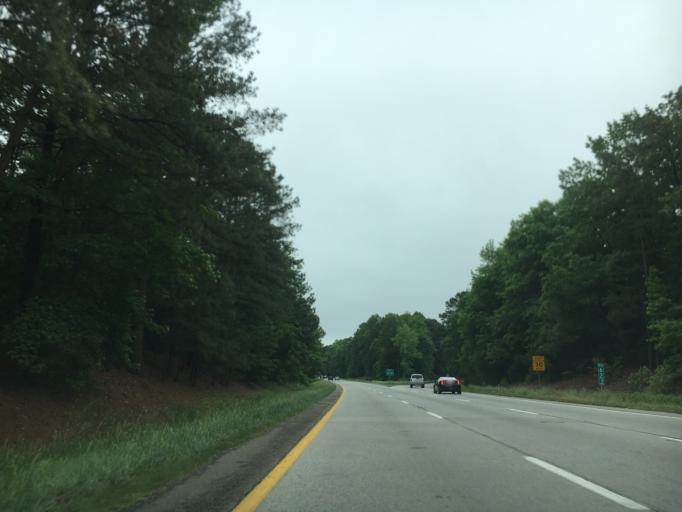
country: US
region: Virginia
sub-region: Chesterfield County
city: Matoaca
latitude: 37.1904
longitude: -77.4883
